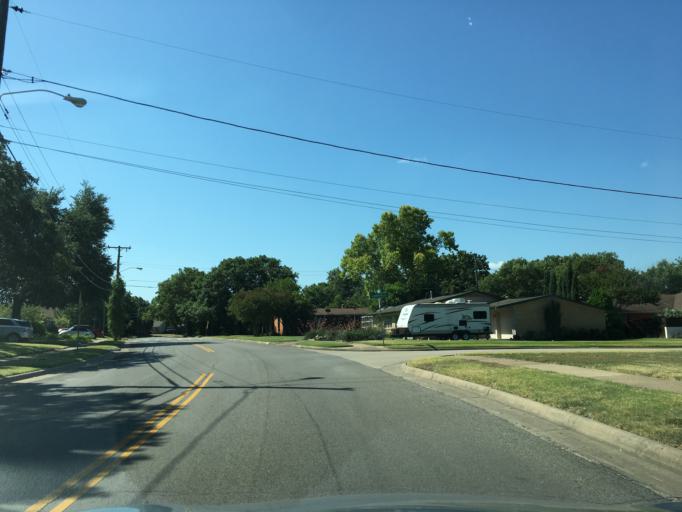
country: US
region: Texas
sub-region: Dallas County
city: Garland
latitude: 32.8690
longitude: -96.6938
